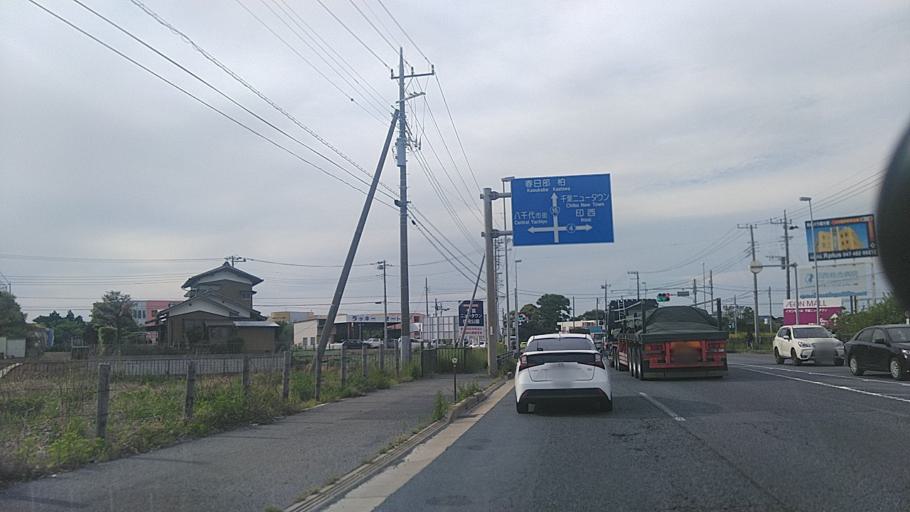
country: JP
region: Chiba
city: Shiroi
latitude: 35.7451
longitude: 140.1210
